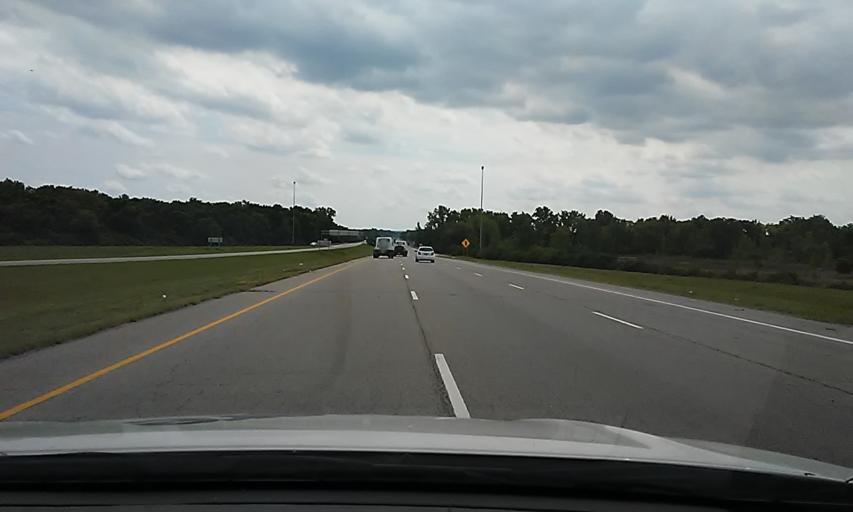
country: US
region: Ohio
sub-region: Clark County
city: Park Layne
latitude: 39.8642
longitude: -84.0564
